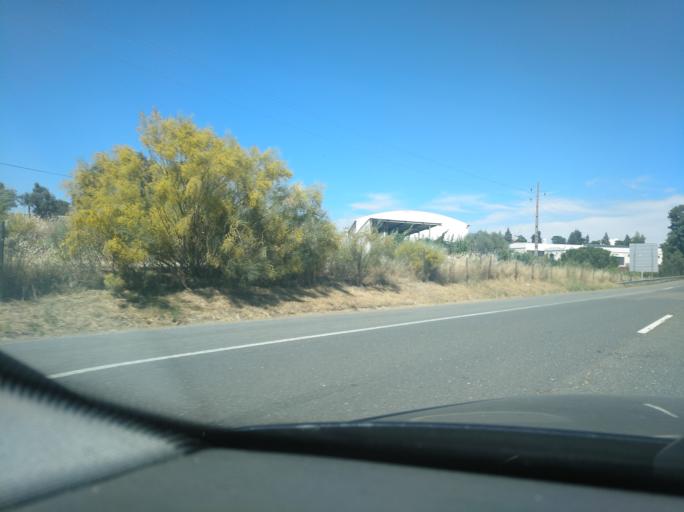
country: PT
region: Beja
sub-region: Castro Verde
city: Castro Verde
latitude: 37.6941
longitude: -8.0943
